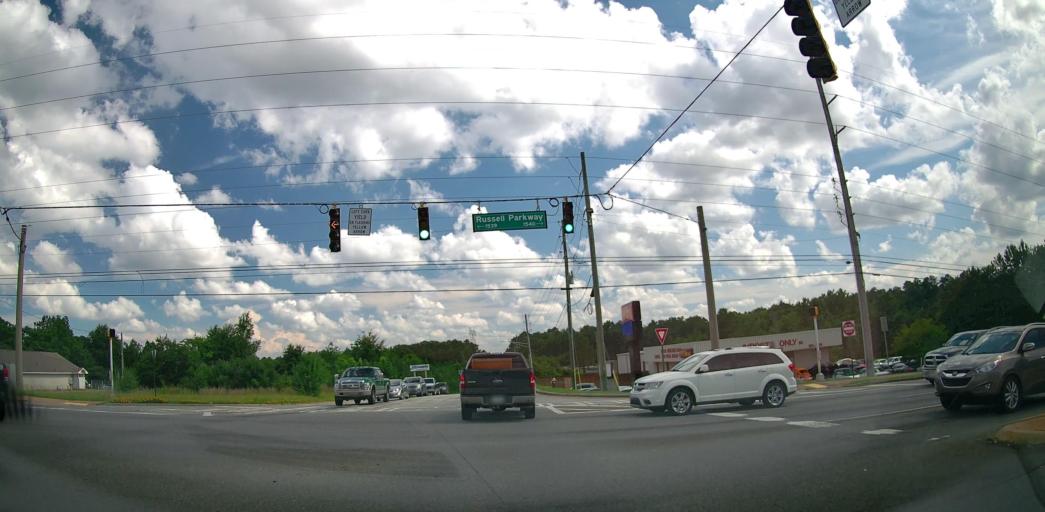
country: US
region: Georgia
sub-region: Houston County
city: Centerville
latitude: 32.5930
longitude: -83.6553
